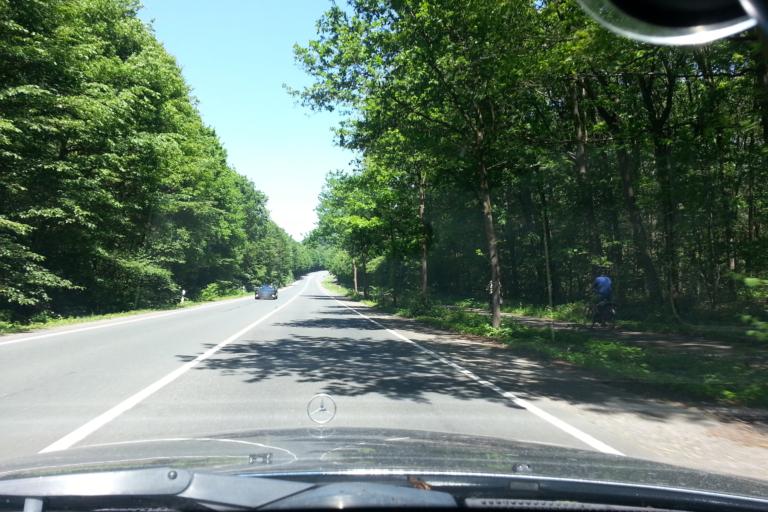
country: DE
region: North Rhine-Westphalia
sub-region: Regierungsbezirk Munster
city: Haltern
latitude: 51.6971
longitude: 7.1899
